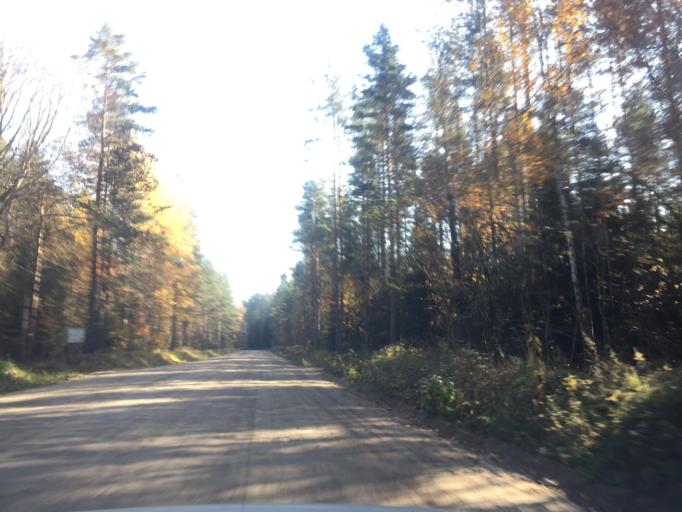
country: RU
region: Leningrad
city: Kuznechnoye
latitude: 61.3155
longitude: 30.0097
